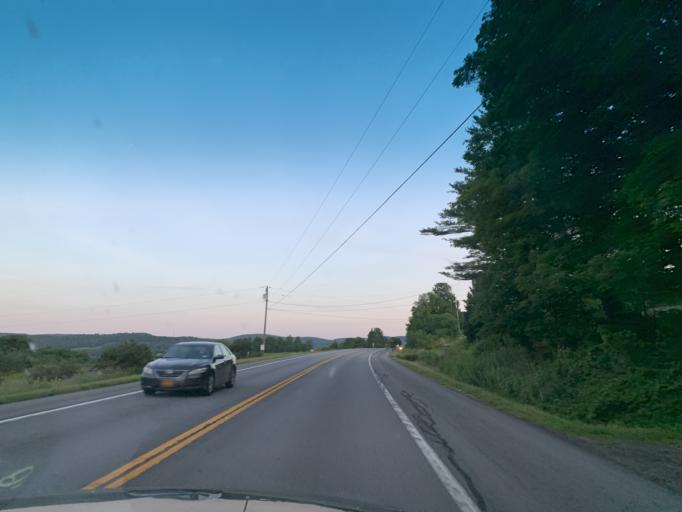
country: US
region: New York
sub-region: Oneida County
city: Waterville
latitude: 42.8298
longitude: -75.2543
